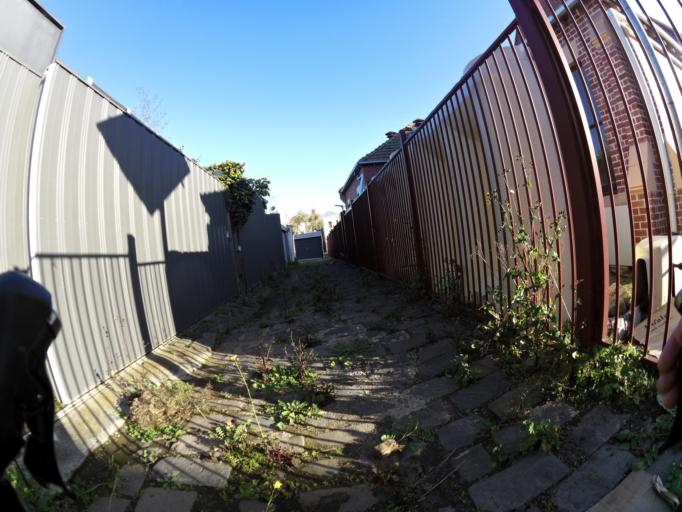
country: AU
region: Victoria
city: Toorak
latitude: -37.8548
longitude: 145.0214
